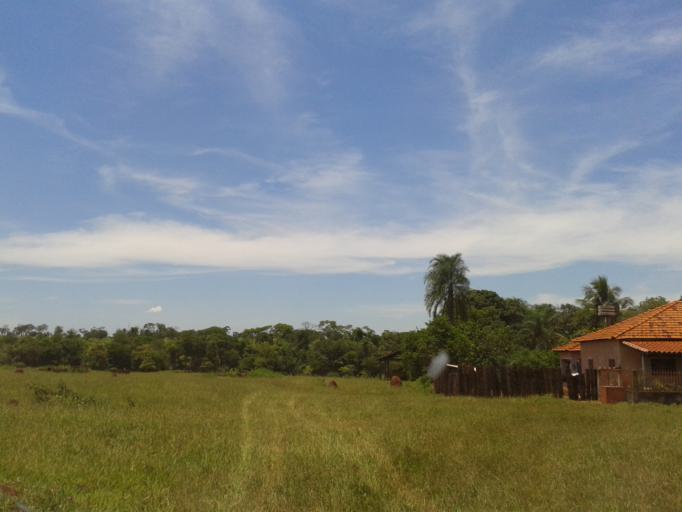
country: BR
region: Minas Gerais
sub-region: Santa Vitoria
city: Santa Vitoria
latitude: -19.1384
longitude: -50.5748
